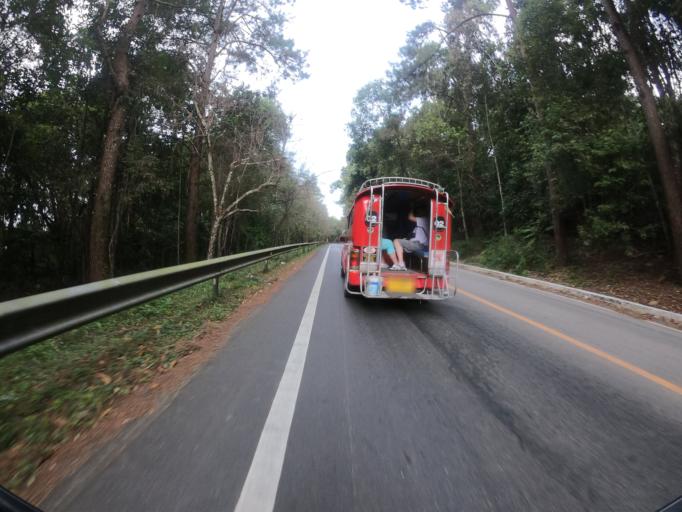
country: TH
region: Chiang Mai
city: Chiang Mai
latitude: 18.8019
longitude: 98.9002
